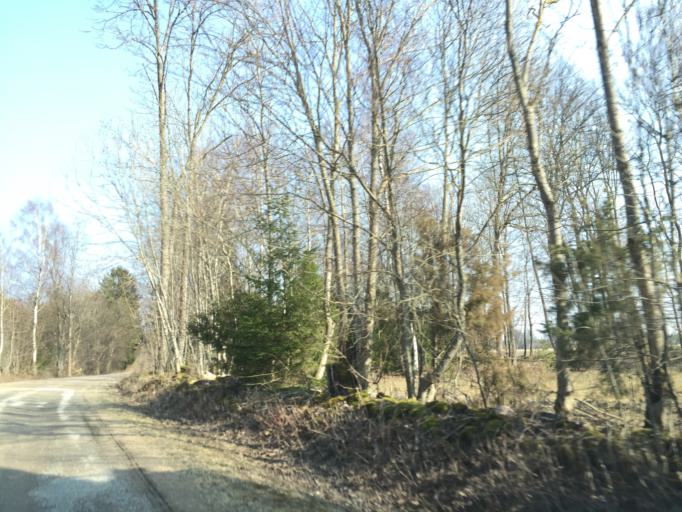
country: EE
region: Saare
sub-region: Kuressaare linn
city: Kuressaare
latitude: 58.3792
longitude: 22.7123
